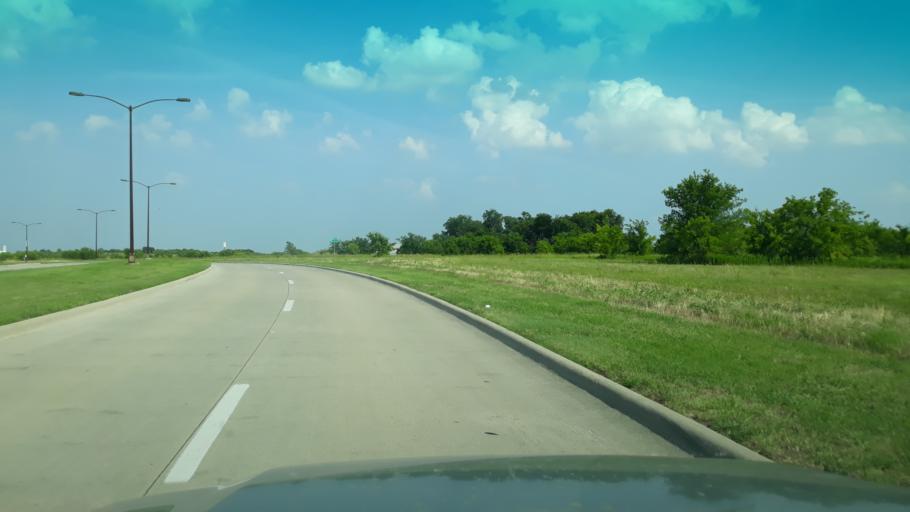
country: US
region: Texas
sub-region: Tarrant County
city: Euless
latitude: 32.8709
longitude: -97.0339
